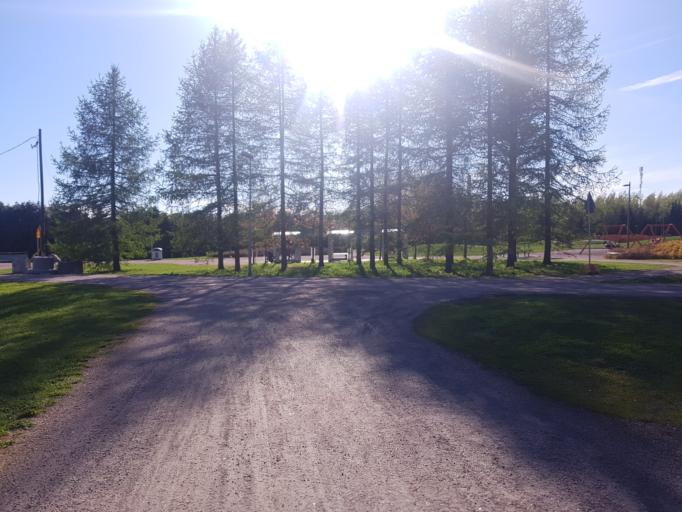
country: FI
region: Uusimaa
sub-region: Helsinki
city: Vantaa
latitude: 60.2364
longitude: 24.9978
